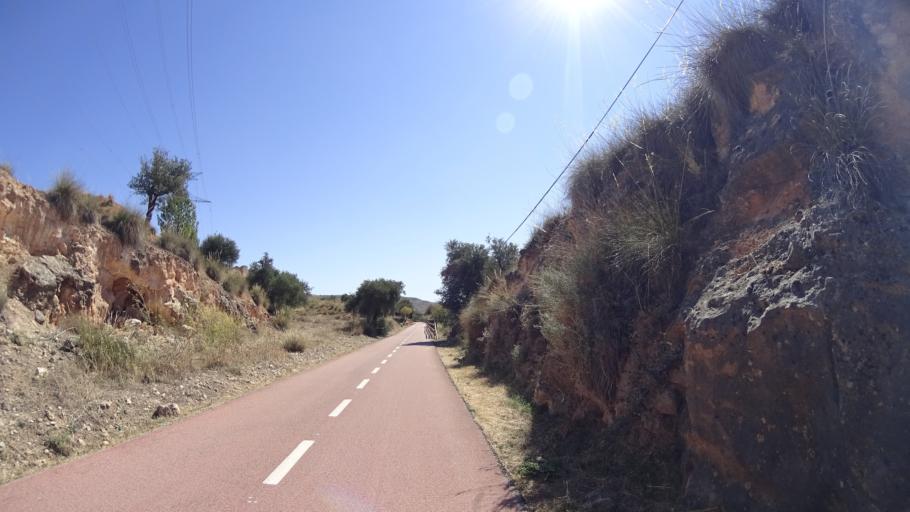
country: ES
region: Madrid
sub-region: Provincia de Madrid
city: Morata de Tajuna
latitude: 40.2304
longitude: -3.4539
